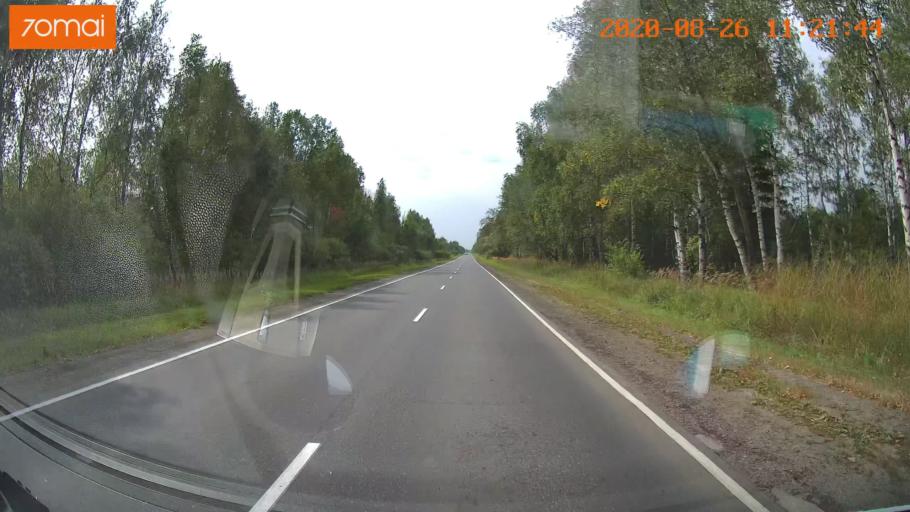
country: RU
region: Rjazan
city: Shilovo
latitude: 54.3727
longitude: 41.0397
